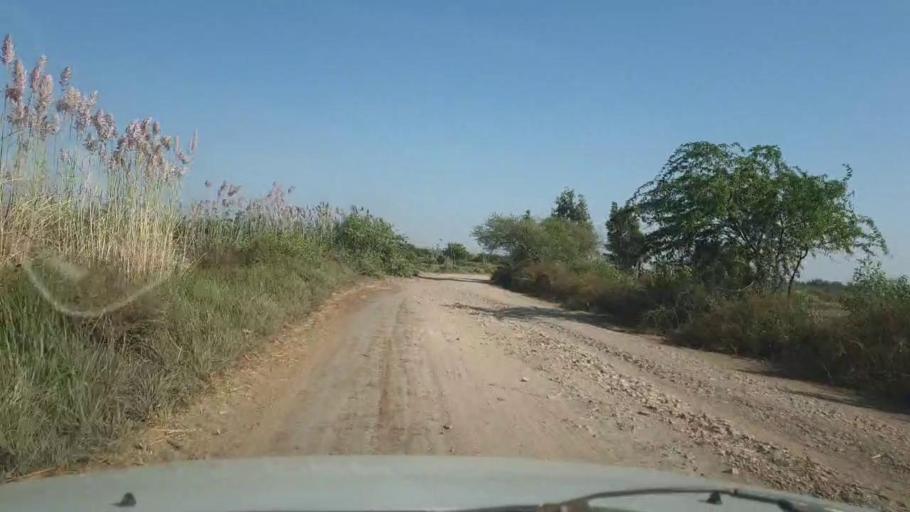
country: PK
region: Sindh
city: Mirpur Sakro
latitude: 24.4864
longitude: 67.8117
